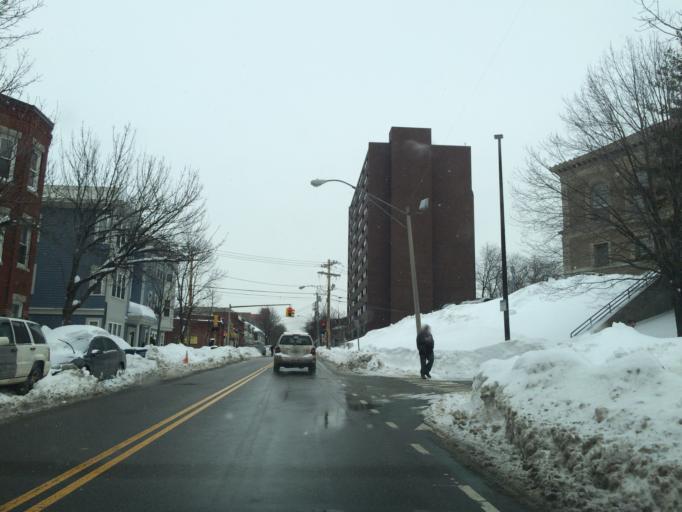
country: US
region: Massachusetts
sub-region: Middlesex County
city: Somerville
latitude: 42.3864
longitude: -71.0944
